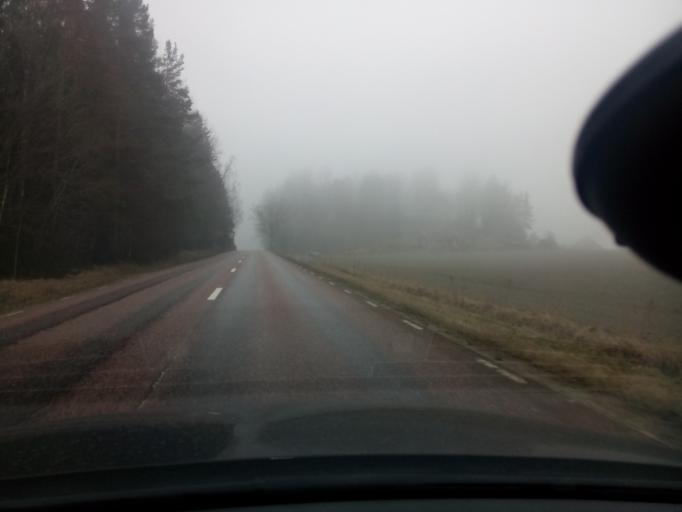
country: SE
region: Soedermanland
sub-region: Nykopings Kommun
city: Nykoping
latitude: 58.8284
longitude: 17.0744
